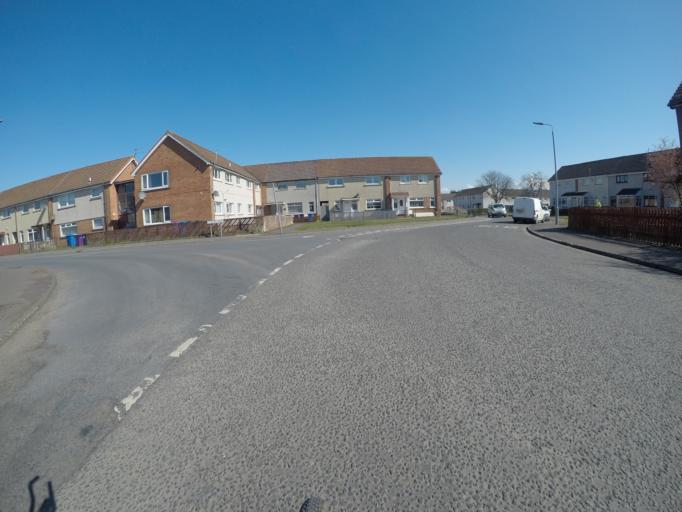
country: GB
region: Scotland
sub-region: North Ayrshire
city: Irvine
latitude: 55.6269
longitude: -4.6602
